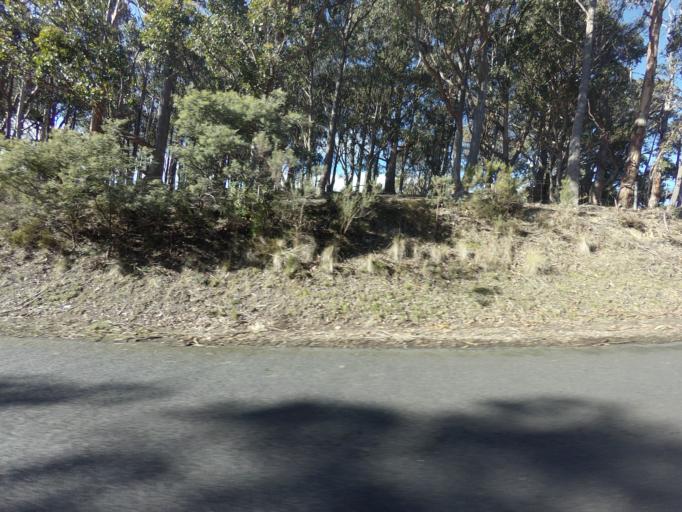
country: AU
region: Tasmania
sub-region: Glenorchy
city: Berriedale
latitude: -42.8280
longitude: 147.1995
